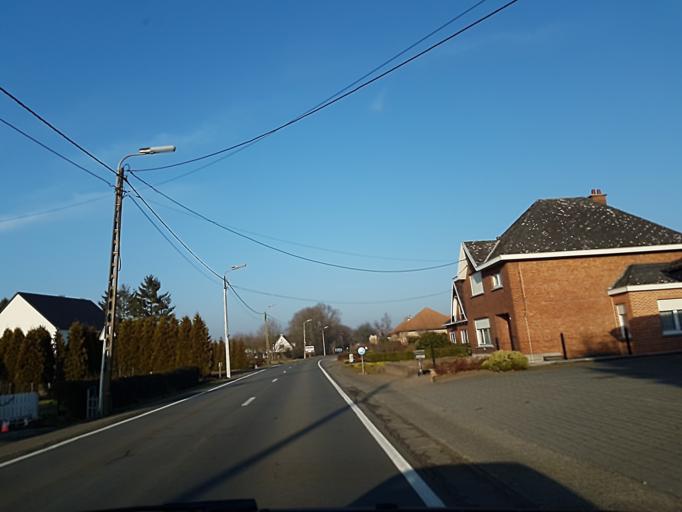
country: BE
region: Flanders
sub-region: Provincie Vlaams-Brabant
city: Tremelo
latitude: 51.0063
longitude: 4.7081
